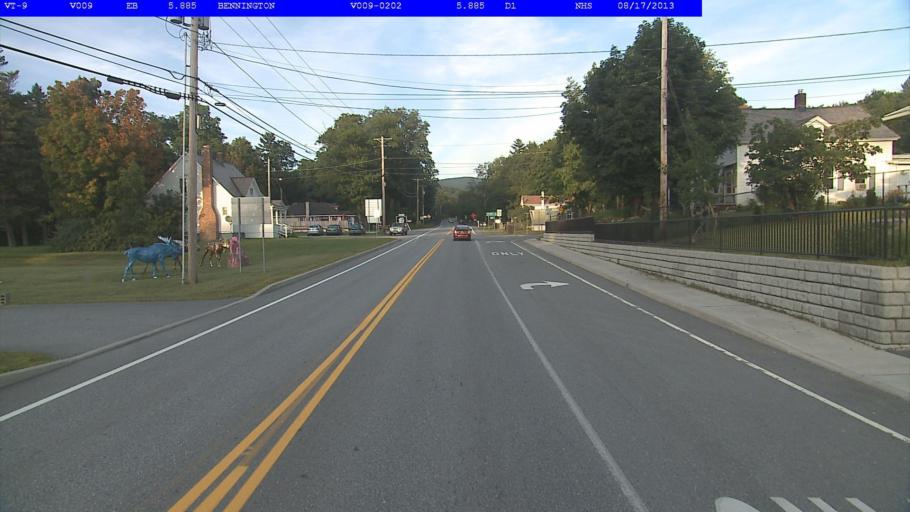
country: US
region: Vermont
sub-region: Bennington County
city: Bennington
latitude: 42.8820
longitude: -73.1689
